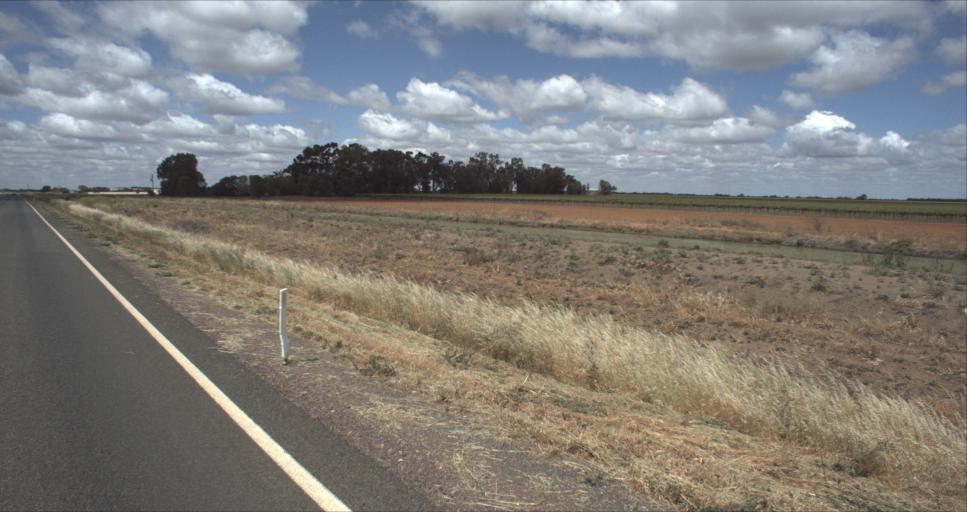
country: AU
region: New South Wales
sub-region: Murrumbidgee Shire
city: Darlington Point
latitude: -34.4818
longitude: 146.1553
